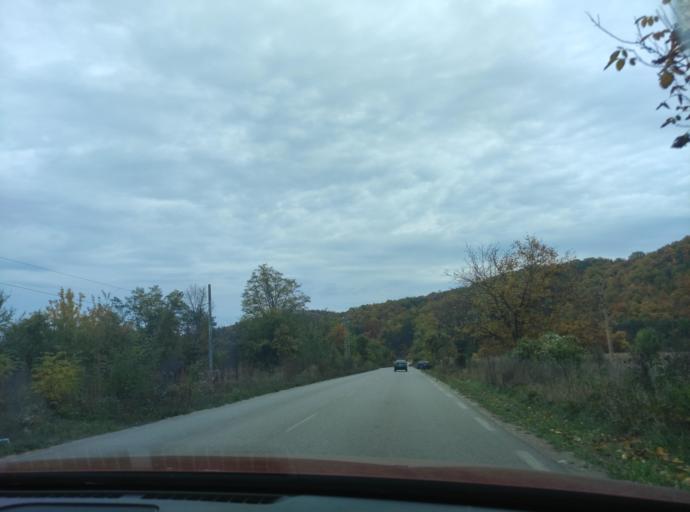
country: BG
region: Montana
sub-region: Obshtina Berkovitsa
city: Berkovitsa
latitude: 43.2591
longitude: 23.1753
